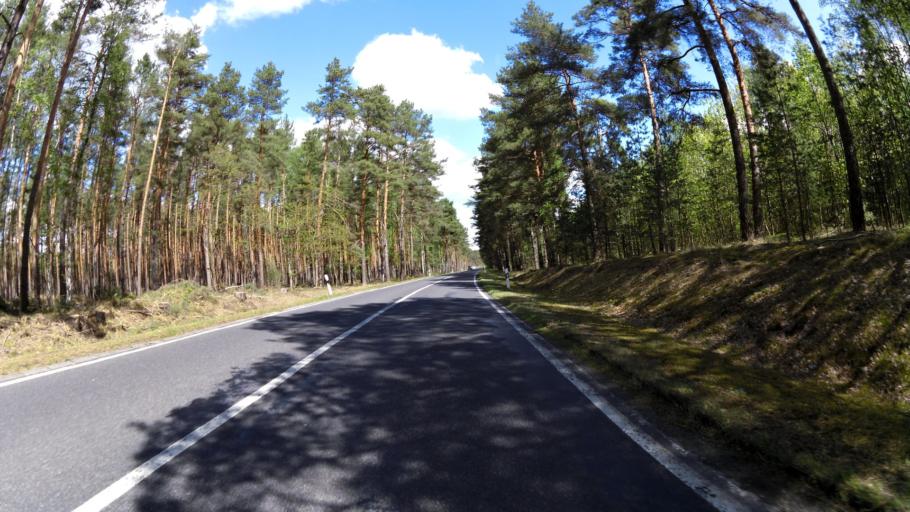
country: DE
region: Brandenburg
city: Wendisch Rietz
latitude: 52.1447
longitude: 13.9686
